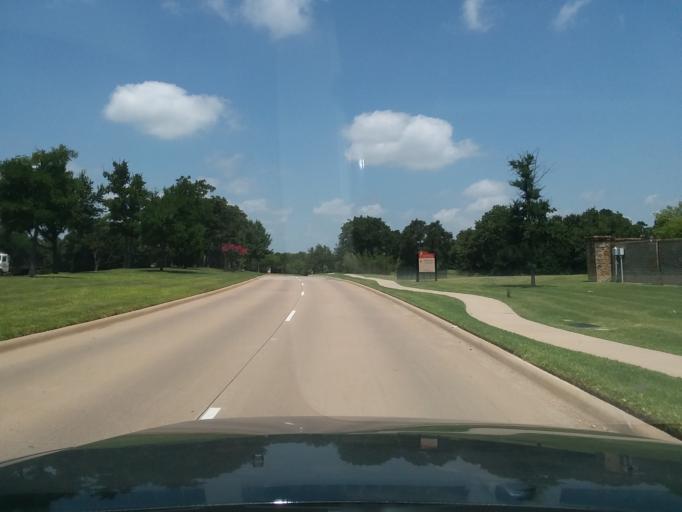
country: US
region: Texas
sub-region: Denton County
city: Copper Canyon
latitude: 33.1013
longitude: -97.1225
